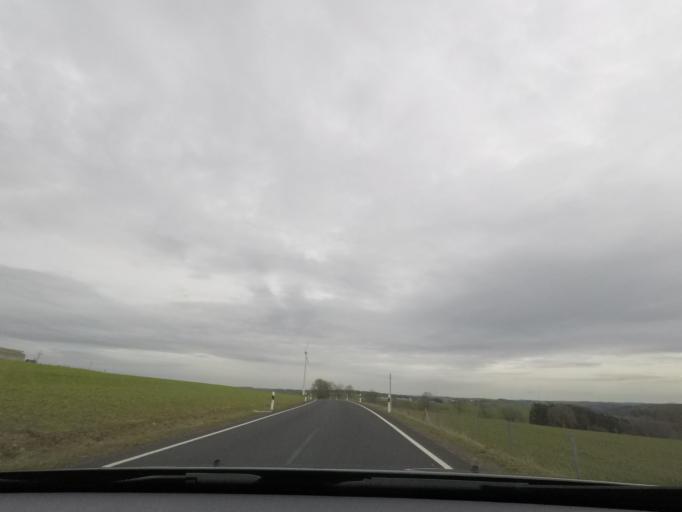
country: LU
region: Diekirch
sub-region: Canton de Clervaux
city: Wincrange
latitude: 50.0168
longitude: 5.8894
